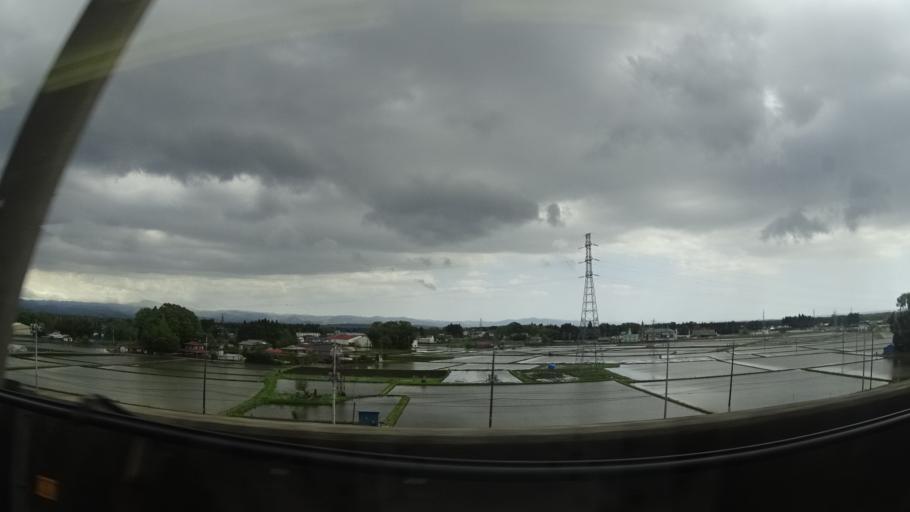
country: JP
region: Tochigi
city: Kuroiso
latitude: 36.9495
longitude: 140.0400
